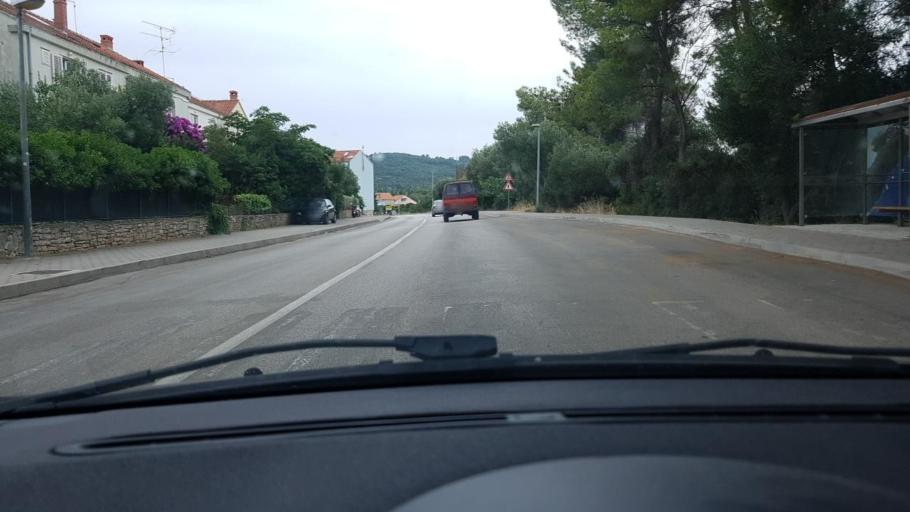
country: HR
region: Dubrovacko-Neretvanska
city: Korcula
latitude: 42.9497
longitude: 17.1427
